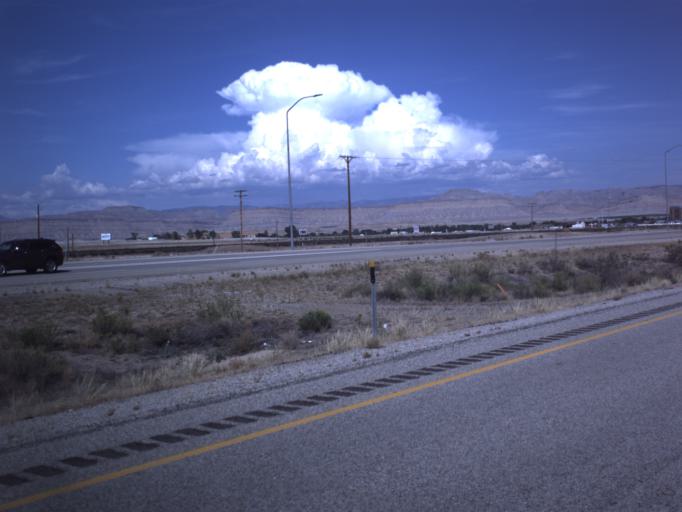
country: US
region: Utah
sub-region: Carbon County
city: East Carbon City
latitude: 38.9914
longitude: -110.1826
